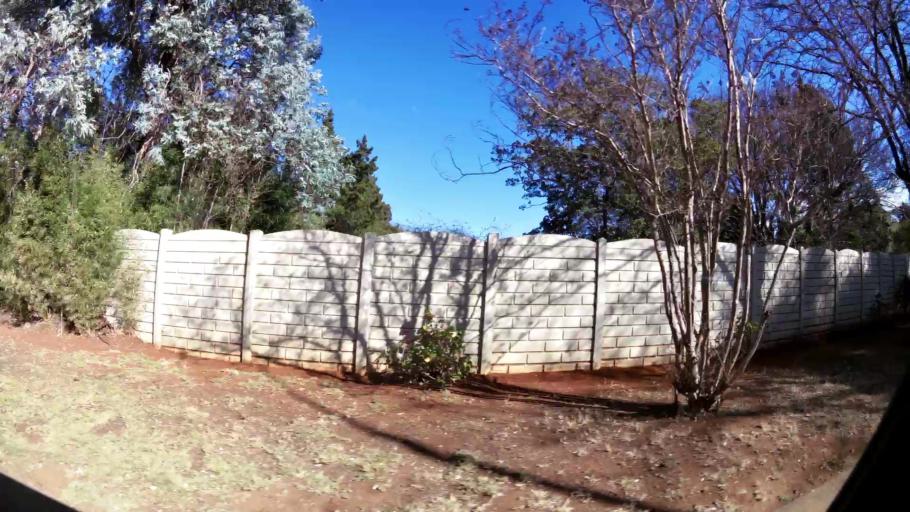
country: ZA
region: Gauteng
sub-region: West Rand District Municipality
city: Carletonville
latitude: -26.3720
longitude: 27.4085
